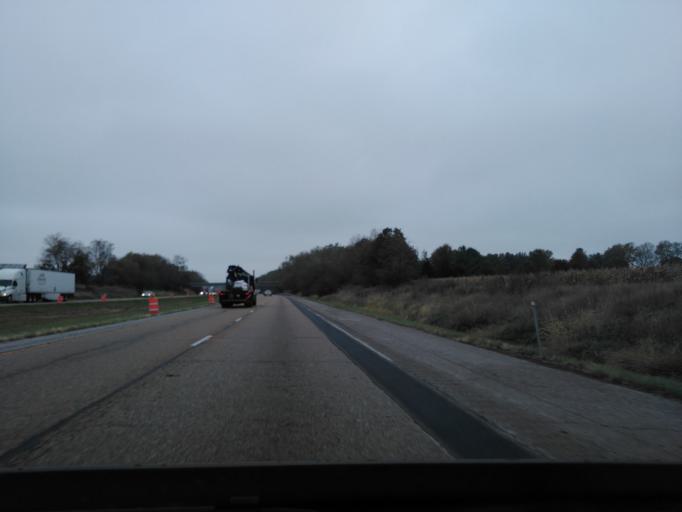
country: US
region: Illinois
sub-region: Madison County
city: Troy
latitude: 38.7558
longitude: -89.8707
